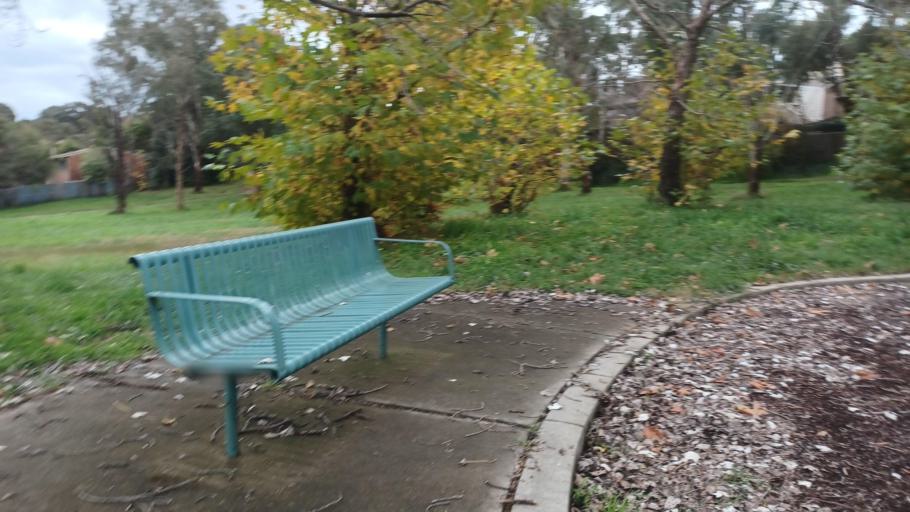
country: AU
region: Australian Capital Territory
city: Belconnen
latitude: -35.1999
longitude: 149.0417
